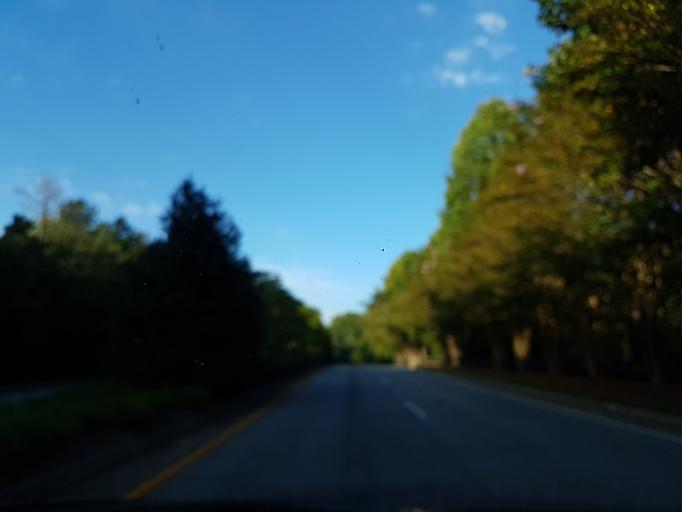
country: US
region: Georgia
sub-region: DeKalb County
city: Doraville
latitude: 33.8766
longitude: -84.2686
